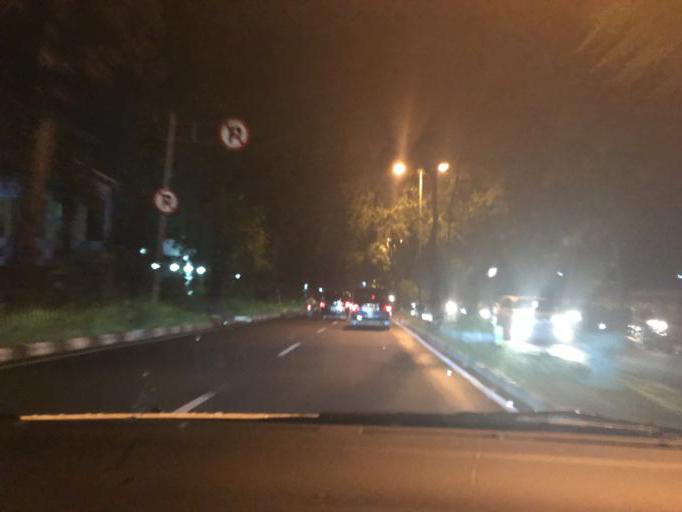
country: ID
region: West Java
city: Bandung
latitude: -6.9104
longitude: 107.6324
